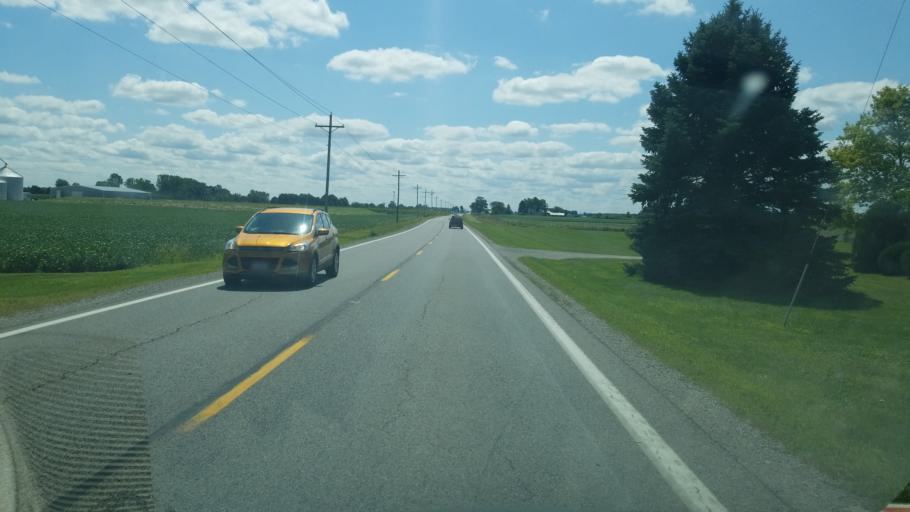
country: US
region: Ohio
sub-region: Fulton County
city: Delta
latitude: 41.6525
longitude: -84.0353
